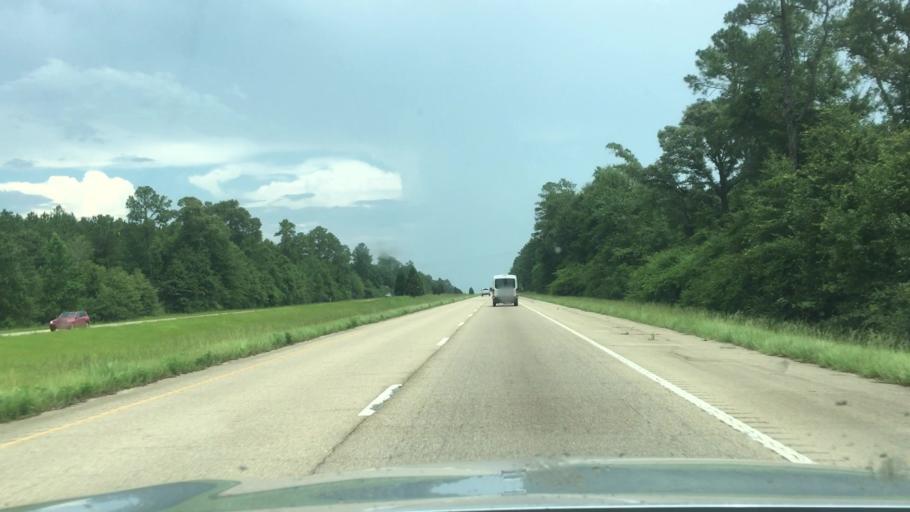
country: US
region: Mississippi
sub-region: Lamar County
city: Lumberton
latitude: 30.9525
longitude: -89.4432
